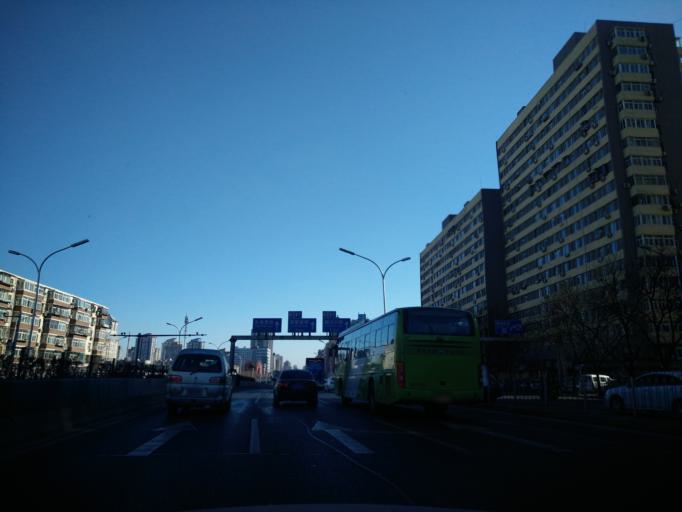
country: CN
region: Beijing
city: Dahongmen
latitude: 39.8557
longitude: 116.3888
